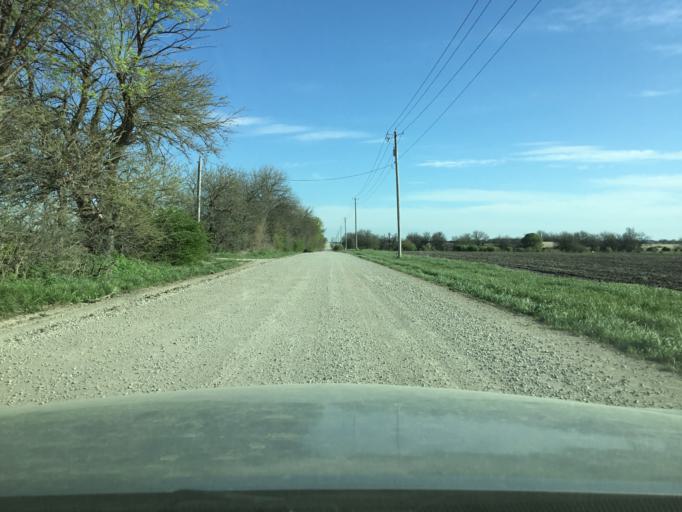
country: US
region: Kansas
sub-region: Neosho County
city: Chanute
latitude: 37.6506
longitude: -95.4893
